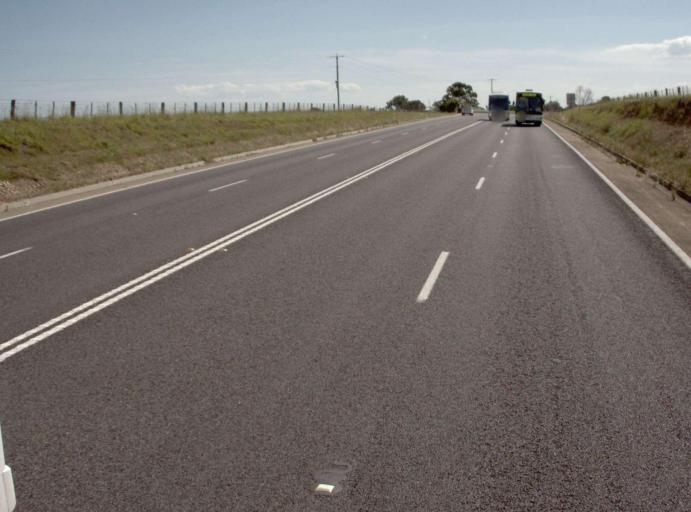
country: AU
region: Victoria
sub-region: East Gippsland
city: Bairnsdale
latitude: -37.8198
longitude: 147.7294
